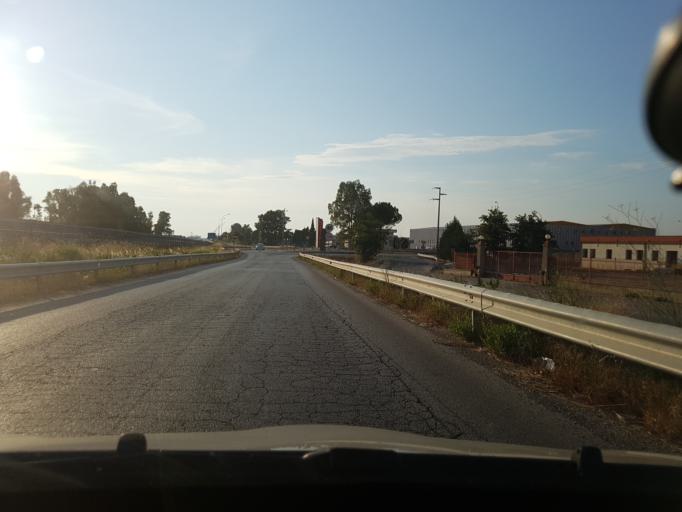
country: IT
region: Apulia
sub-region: Provincia di Foggia
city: Carapelle
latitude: 41.4017
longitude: 15.6509
